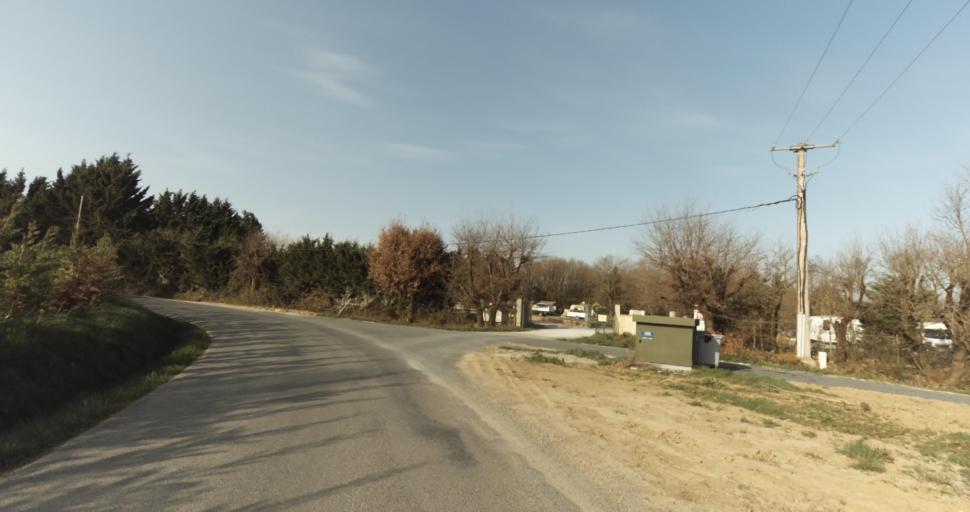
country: FR
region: Midi-Pyrenees
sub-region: Departement du Tarn
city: Saint-Sulpice-la-Pointe
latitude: 43.7471
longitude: 1.6871
